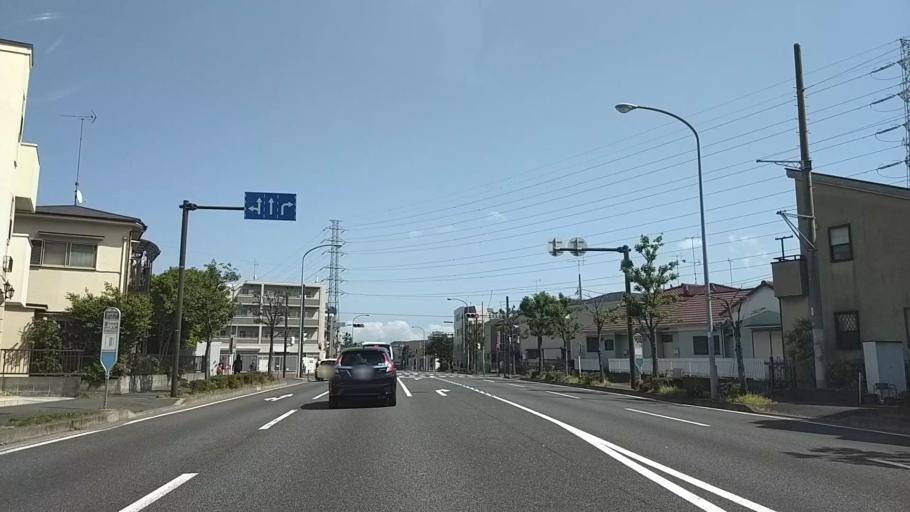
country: JP
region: Kanagawa
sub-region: Kawasaki-shi
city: Kawasaki
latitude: 35.5472
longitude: 139.6303
